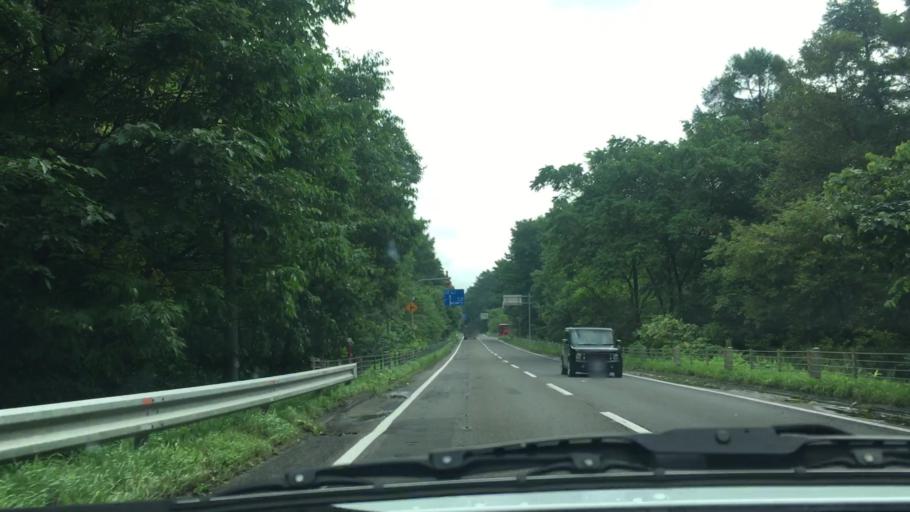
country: JP
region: Hokkaido
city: Chitose
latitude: 42.9446
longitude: 141.7426
